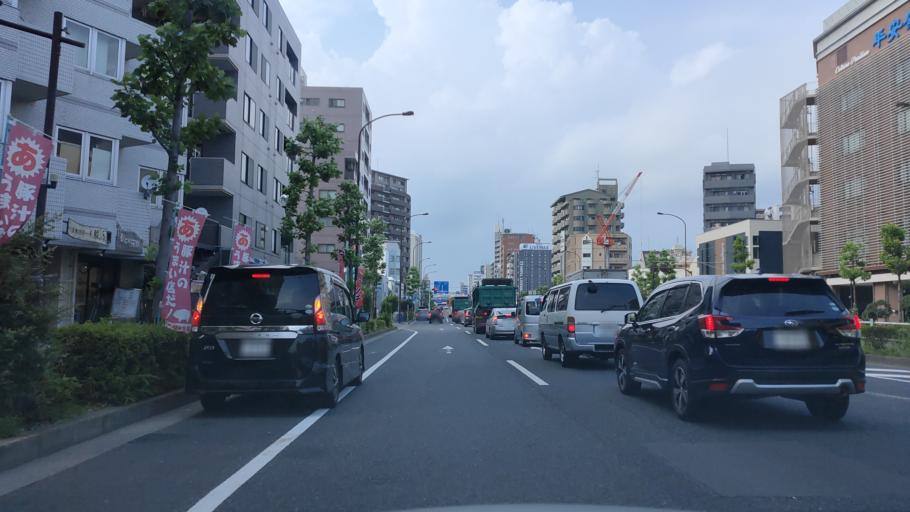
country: JP
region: Tokyo
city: Urayasu
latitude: 35.6579
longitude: 139.8726
